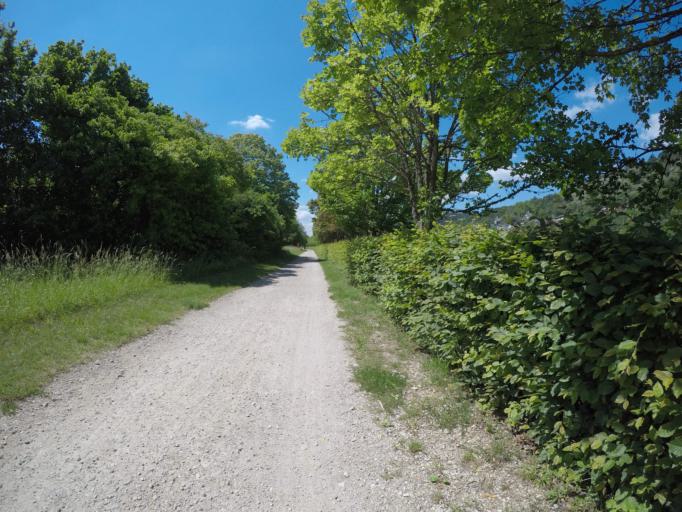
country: DE
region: Bavaria
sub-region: Lower Bavaria
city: Ihrlerstein
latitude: 48.9227
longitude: 11.8641
